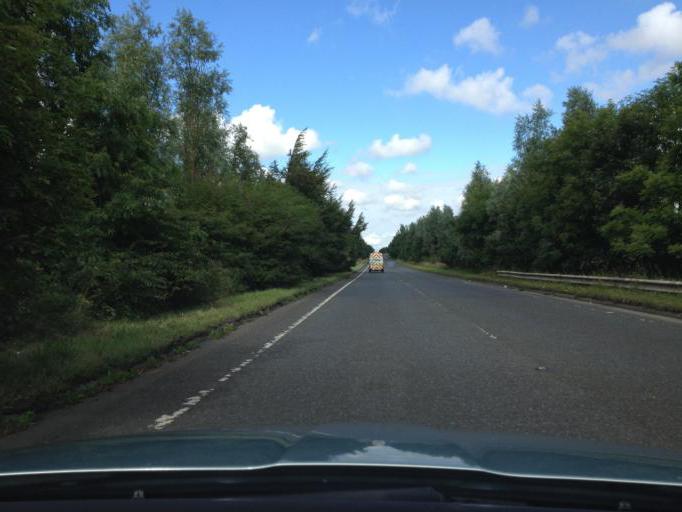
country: GB
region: Scotland
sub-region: West Lothian
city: Whitburn
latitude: 55.8828
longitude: -3.6658
